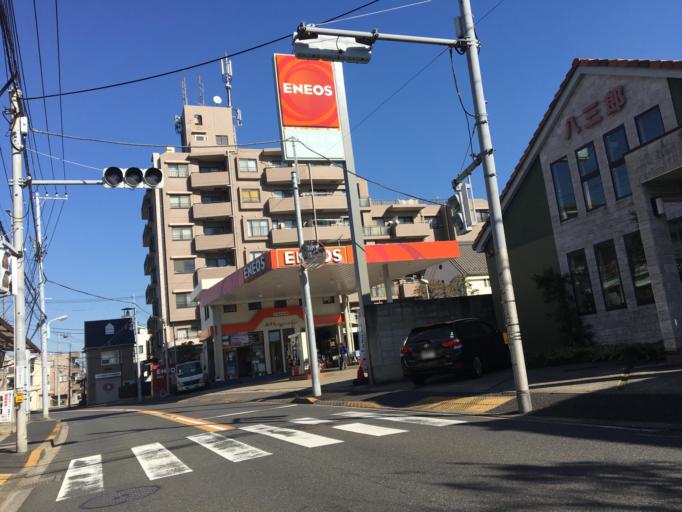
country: JP
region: Tokyo
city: Urayasu
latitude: 35.6856
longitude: 139.8969
